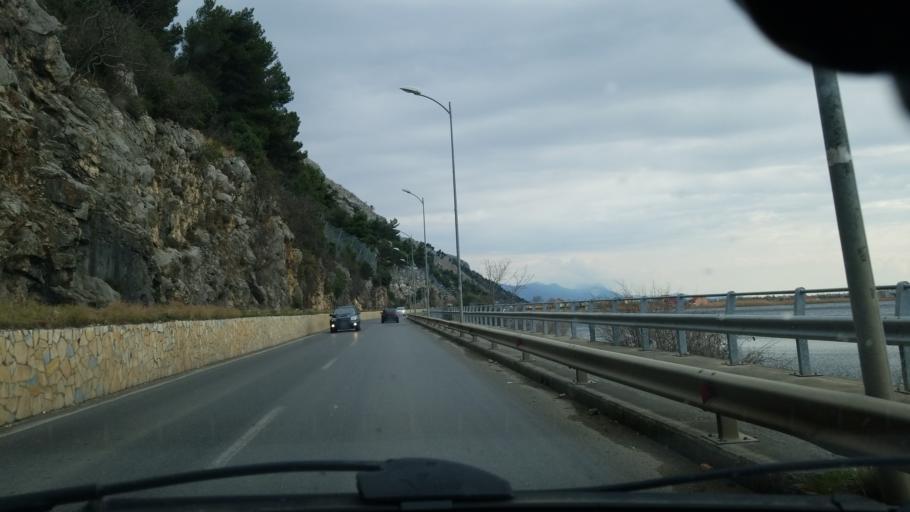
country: AL
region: Lezhe
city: Shengjin
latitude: 41.8049
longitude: 19.6127
